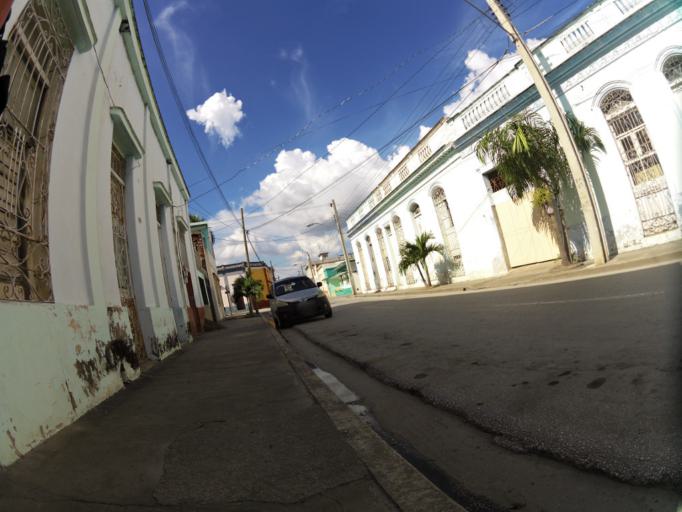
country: CU
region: Granma
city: Bayamo
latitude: 20.3710
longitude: -76.6483
